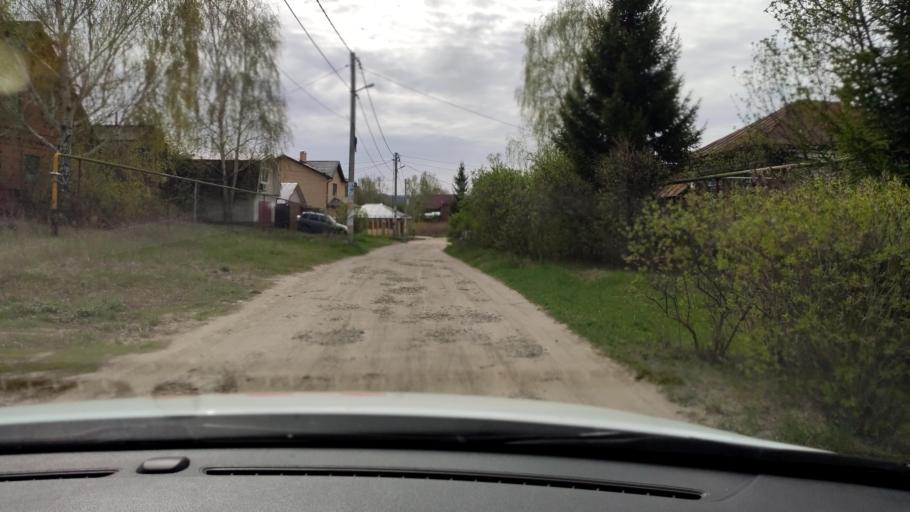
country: RU
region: Tatarstan
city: Osinovo
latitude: 55.8085
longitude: 48.8850
